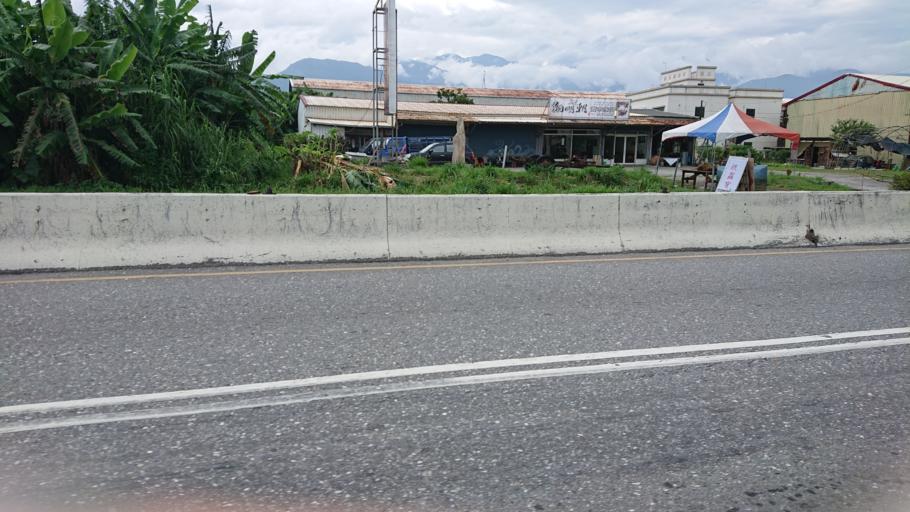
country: TW
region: Taiwan
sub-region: Hualien
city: Hualian
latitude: 23.9435
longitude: 121.5960
